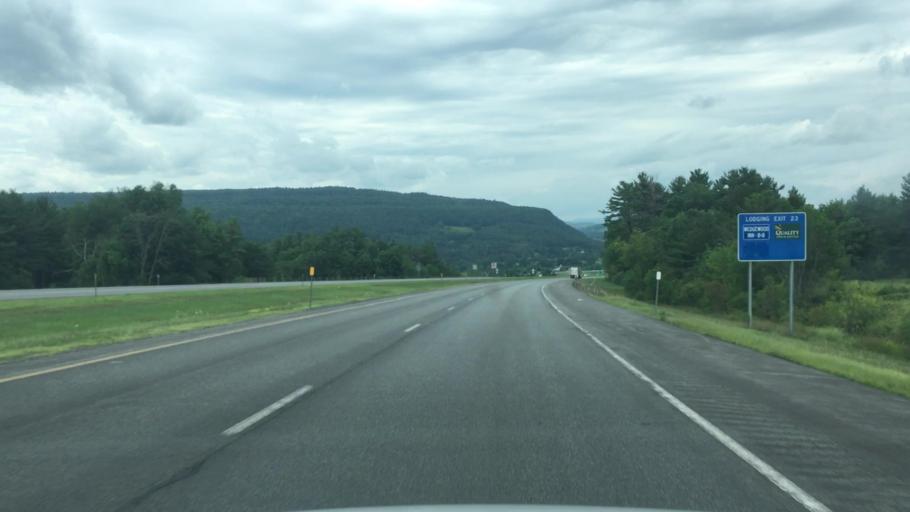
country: US
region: New York
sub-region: Schoharie County
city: Schoharie
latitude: 42.7103
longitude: -74.2979
